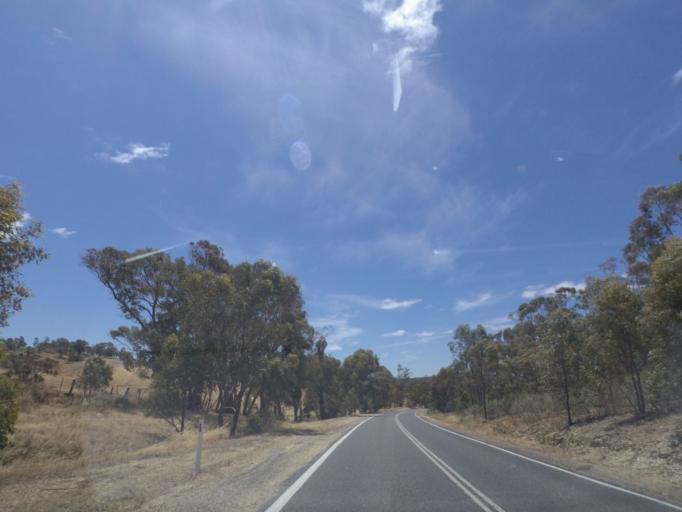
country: AU
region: Victoria
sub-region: Mount Alexander
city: Castlemaine
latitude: -37.2041
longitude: 144.1415
